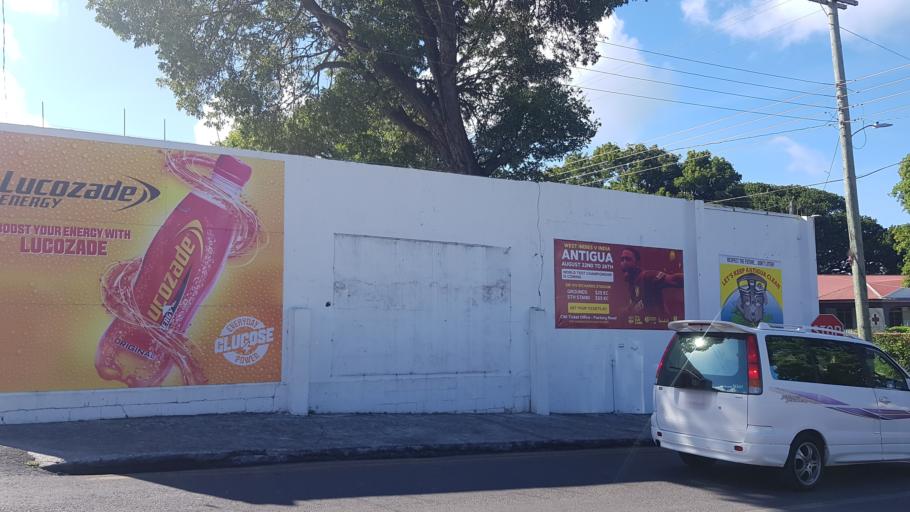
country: AG
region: Saint John
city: Saint John's
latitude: 17.1232
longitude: -61.8384
